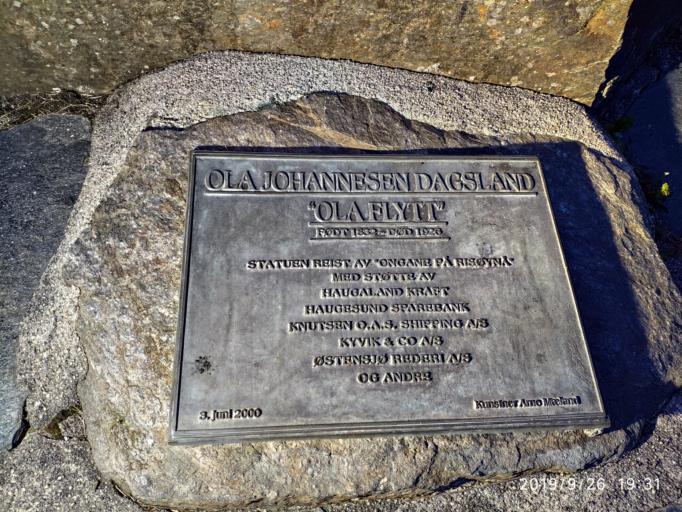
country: NO
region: Rogaland
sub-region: Haugesund
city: Haugesund
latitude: 59.4099
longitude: 5.2682
